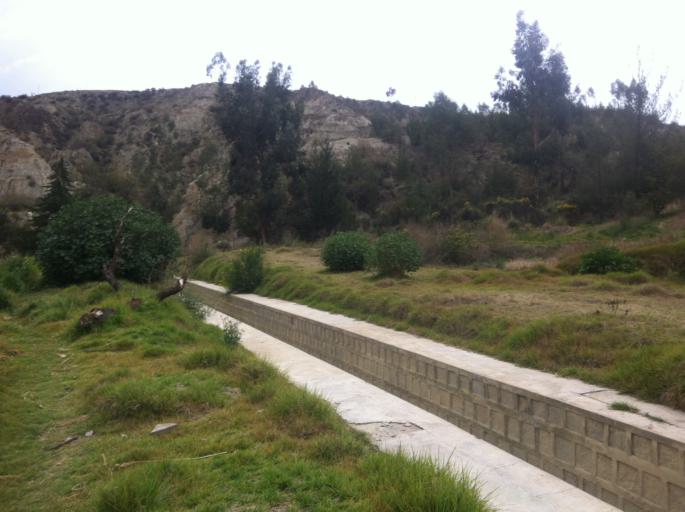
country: BO
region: La Paz
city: La Paz
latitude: -16.5357
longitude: -68.0653
